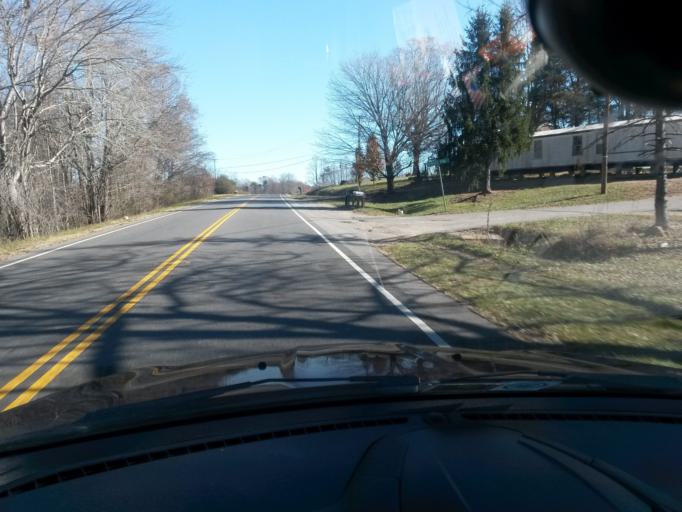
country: US
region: Virginia
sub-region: Henry County
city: Bassett
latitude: 36.7597
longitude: -80.0521
